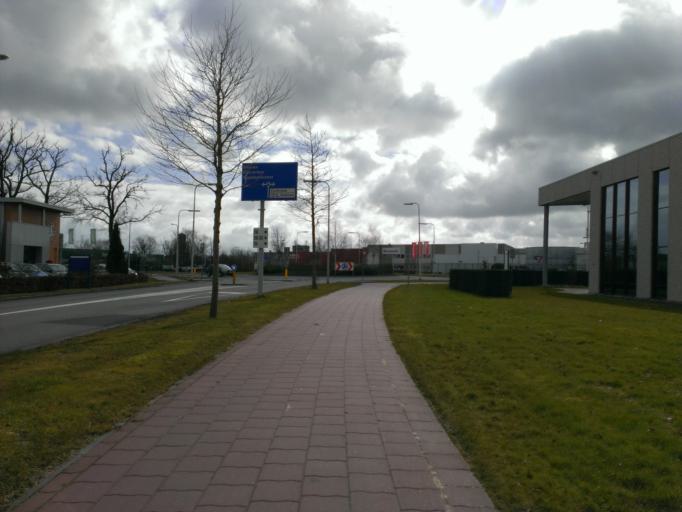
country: NL
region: Drenthe
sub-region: Gemeente Hoogeveen
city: Hoogeveen
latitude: 52.7322
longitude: 6.4885
